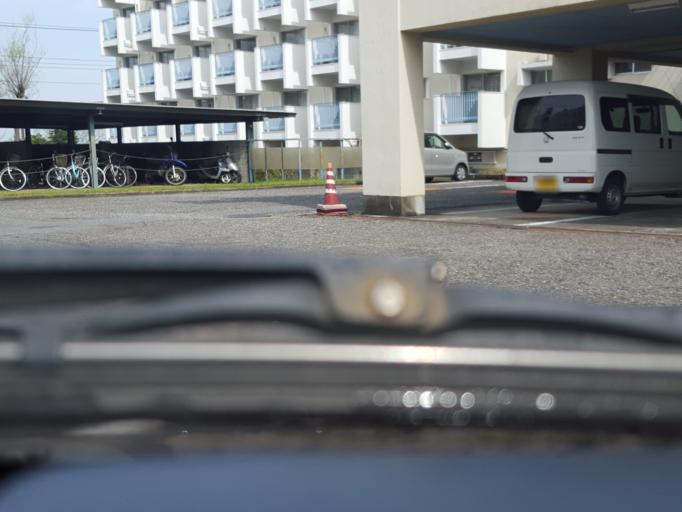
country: JP
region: Chiba
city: Ichihara
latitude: 35.4495
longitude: 140.0558
